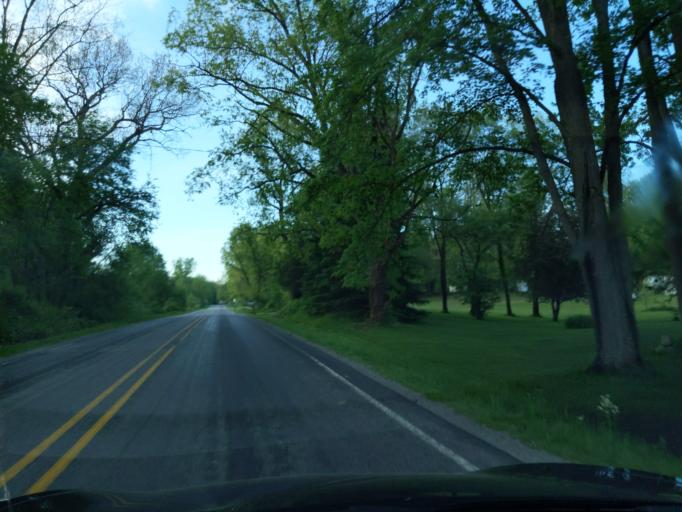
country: US
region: Michigan
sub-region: Ingham County
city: Leslie
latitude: 42.4781
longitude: -84.3170
